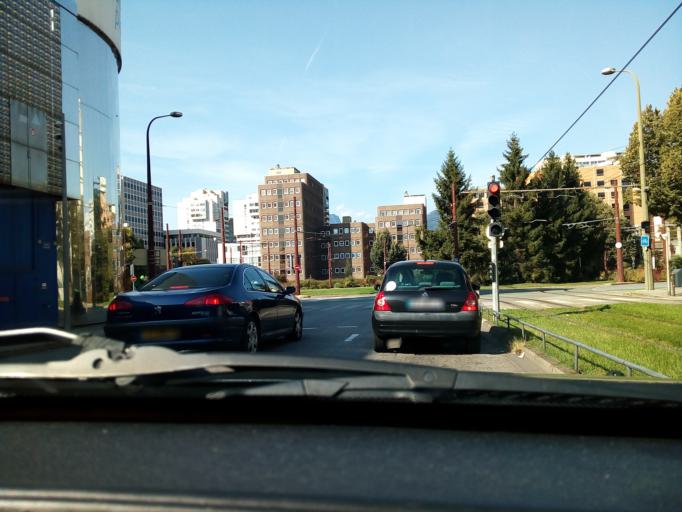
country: FR
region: Rhone-Alpes
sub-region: Departement de l'Isere
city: Echirolles
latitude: 45.1584
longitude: 5.7338
